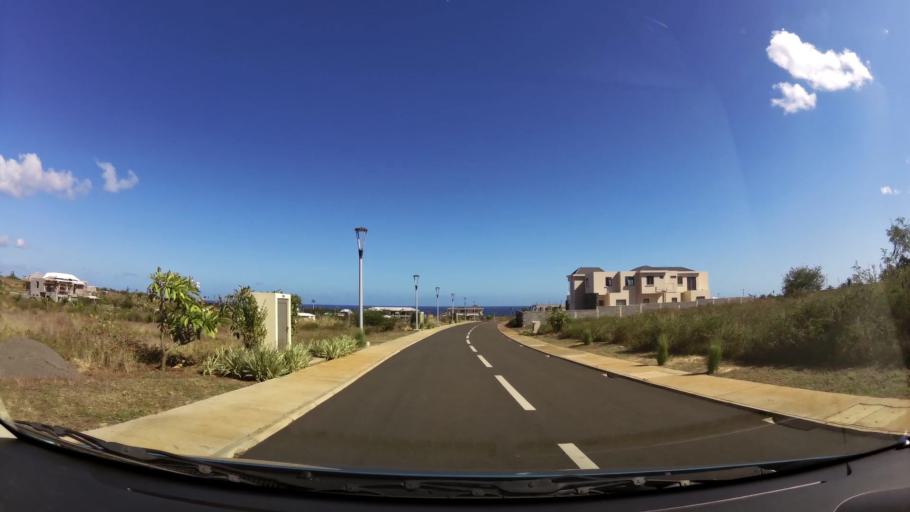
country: MU
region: Black River
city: Flic en Flac
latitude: -20.2689
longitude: 57.3842
